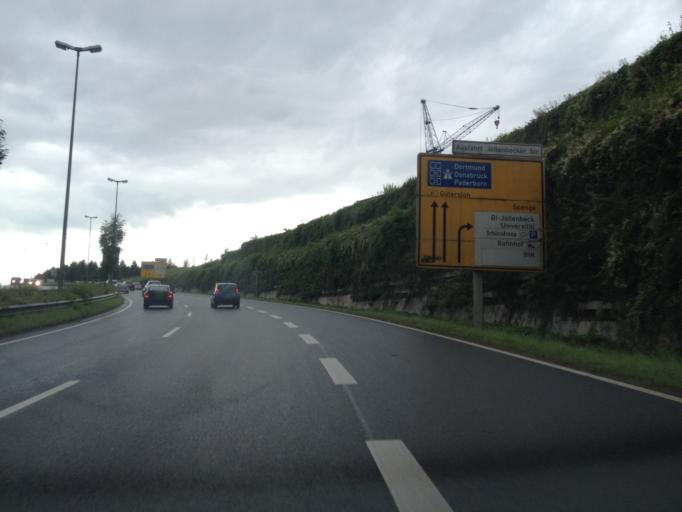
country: DE
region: North Rhine-Westphalia
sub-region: Regierungsbezirk Detmold
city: Bielefeld
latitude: 52.0319
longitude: 8.5316
